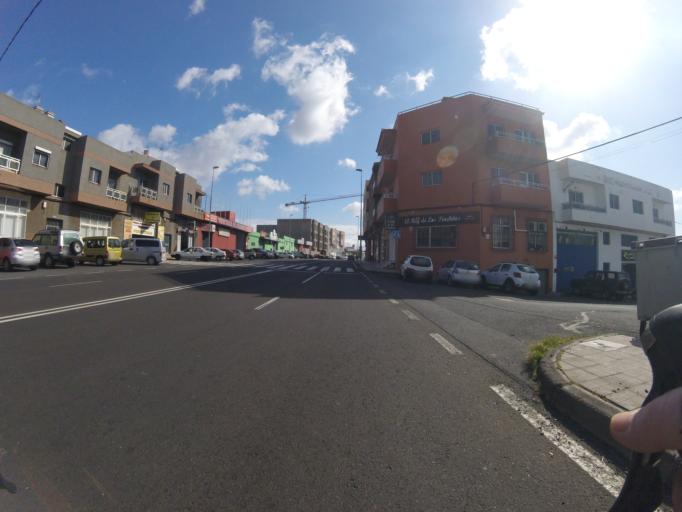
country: ES
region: Canary Islands
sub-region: Provincia de Santa Cruz de Tenerife
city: La Laguna
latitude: 28.4234
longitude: -16.3186
